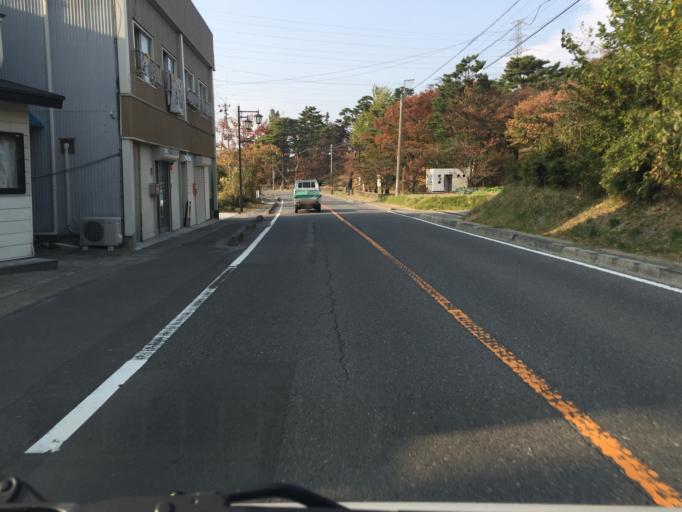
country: JP
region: Fukushima
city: Koriyama
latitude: 37.4534
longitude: 140.3901
